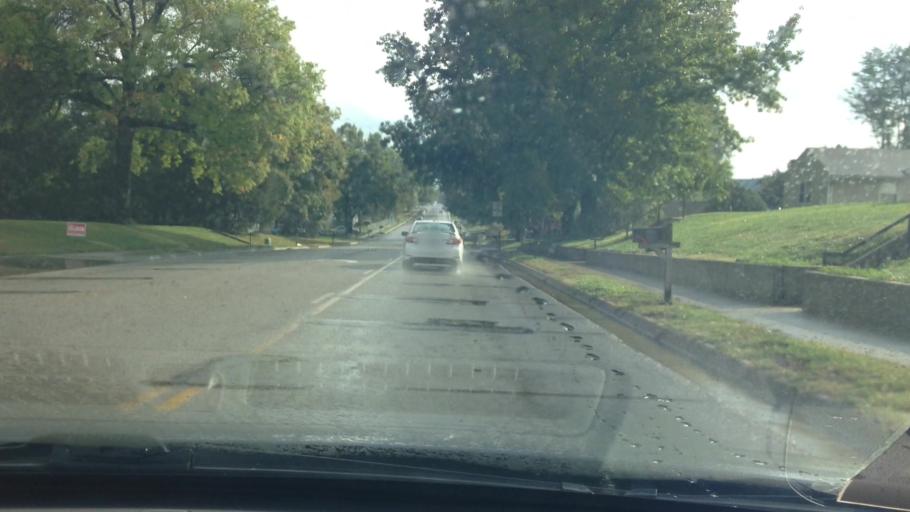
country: US
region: Kansas
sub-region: Leavenworth County
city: Leavenworth
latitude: 39.3002
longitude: -94.9276
